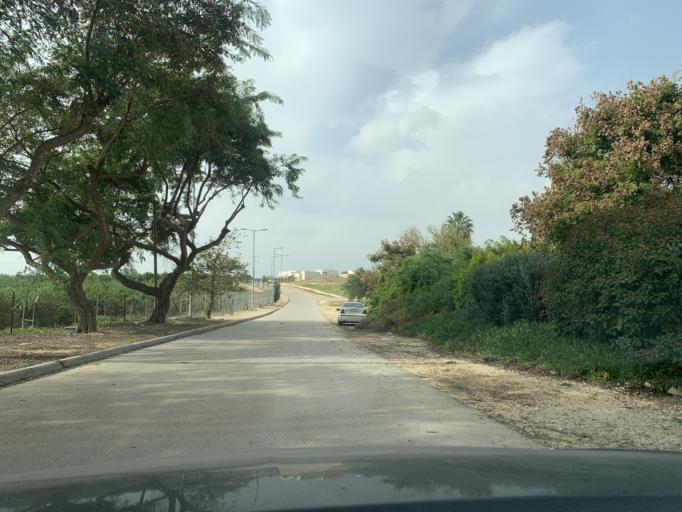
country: IL
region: Central District
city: Tirah
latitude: 32.2145
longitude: 34.9362
